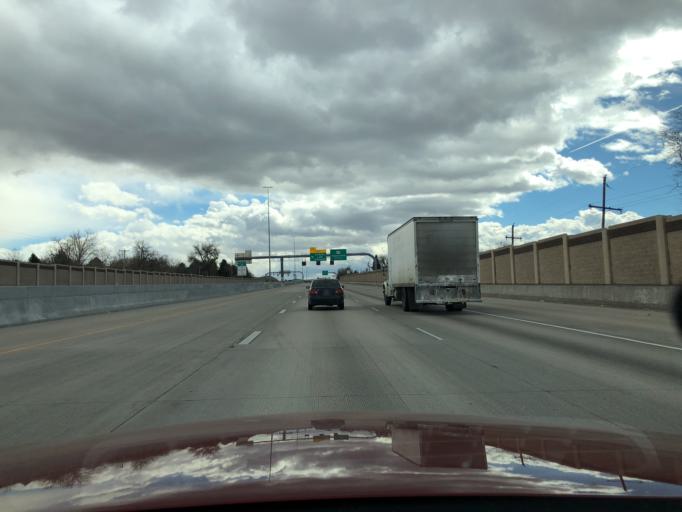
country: US
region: Colorado
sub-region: Adams County
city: Westminster
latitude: 39.8475
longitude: -105.0453
